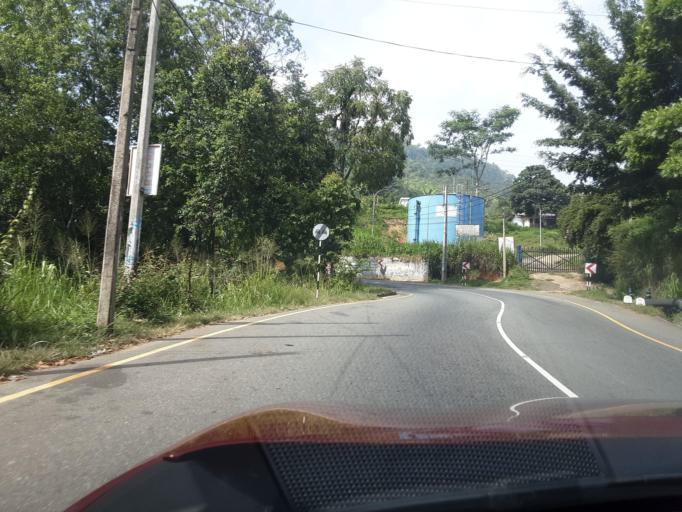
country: LK
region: Uva
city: Badulla
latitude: 6.9823
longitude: 81.0797
